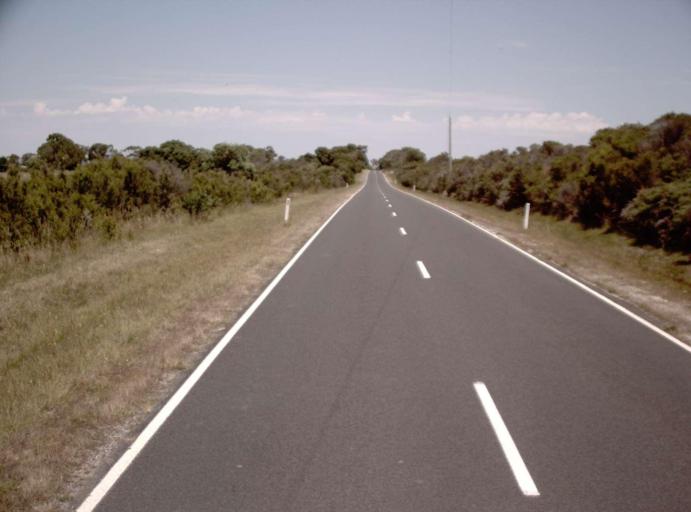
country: AU
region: Victoria
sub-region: Bass Coast
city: North Wonthaggi
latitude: -38.6458
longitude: 145.9417
